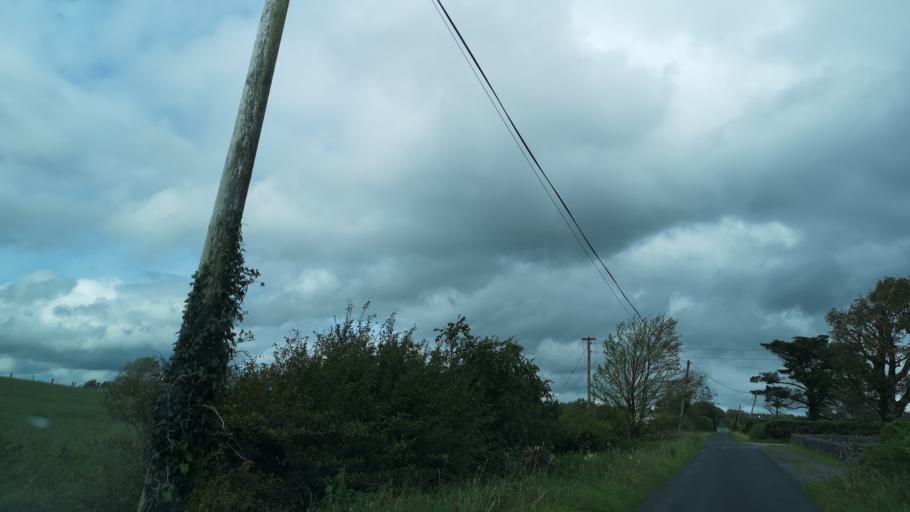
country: IE
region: Connaught
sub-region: County Galway
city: Athenry
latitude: 53.2862
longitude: -8.6660
